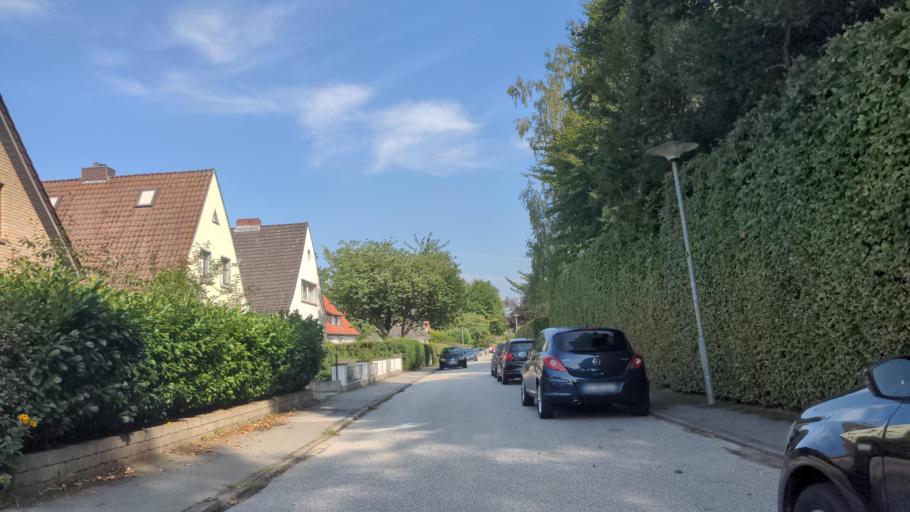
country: DE
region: Schleswig-Holstein
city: Luebeck
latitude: 53.8887
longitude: 10.7140
